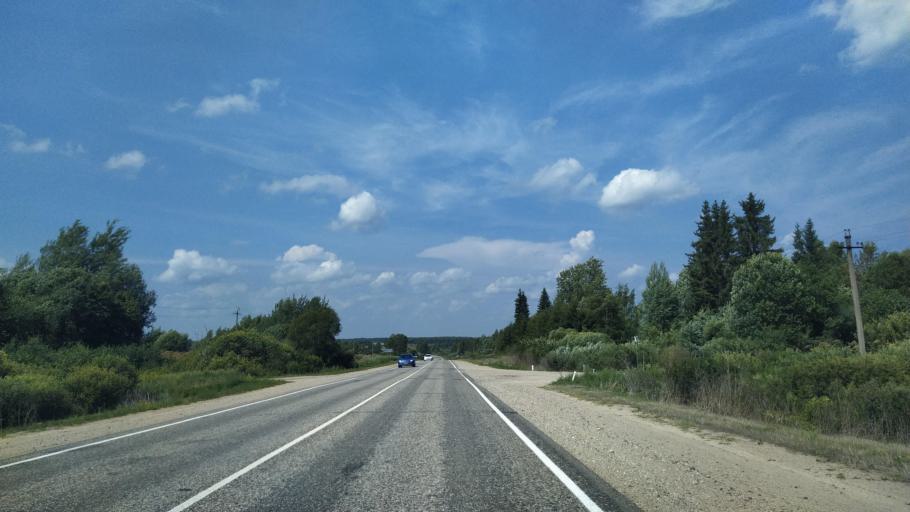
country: RU
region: Pskov
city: Pushkinskiye Gory
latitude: 57.0192
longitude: 28.8776
